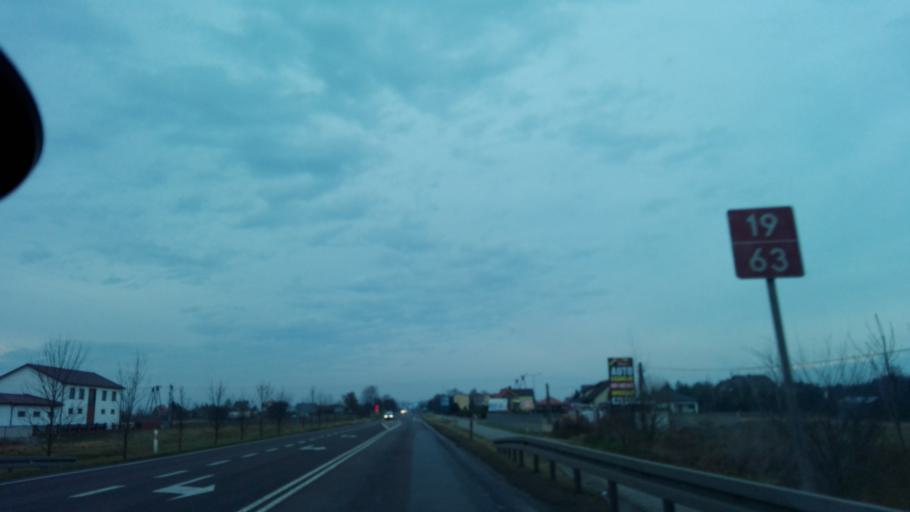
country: PL
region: Lublin Voivodeship
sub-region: Powiat radzynski
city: Radzyn Podlaski
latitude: 51.7778
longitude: 22.5909
